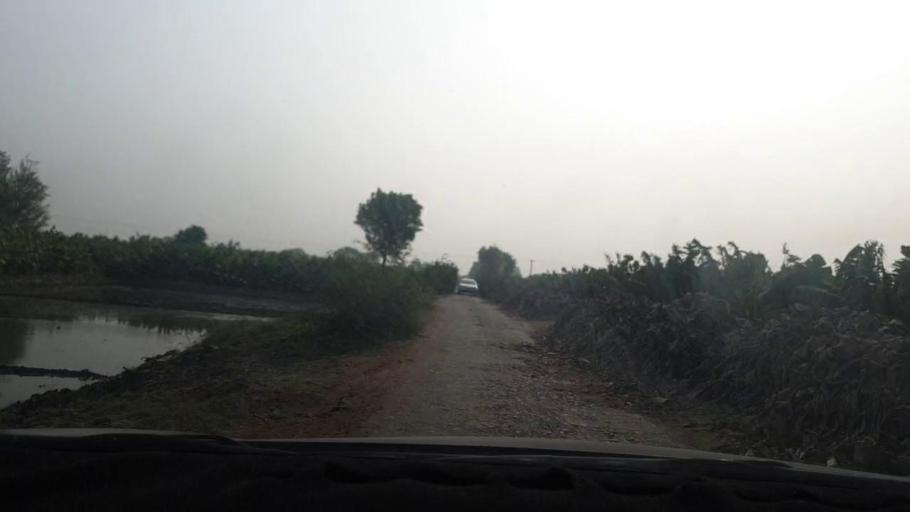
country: PK
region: Sindh
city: Matiari
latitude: 25.5922
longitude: 68.5451
